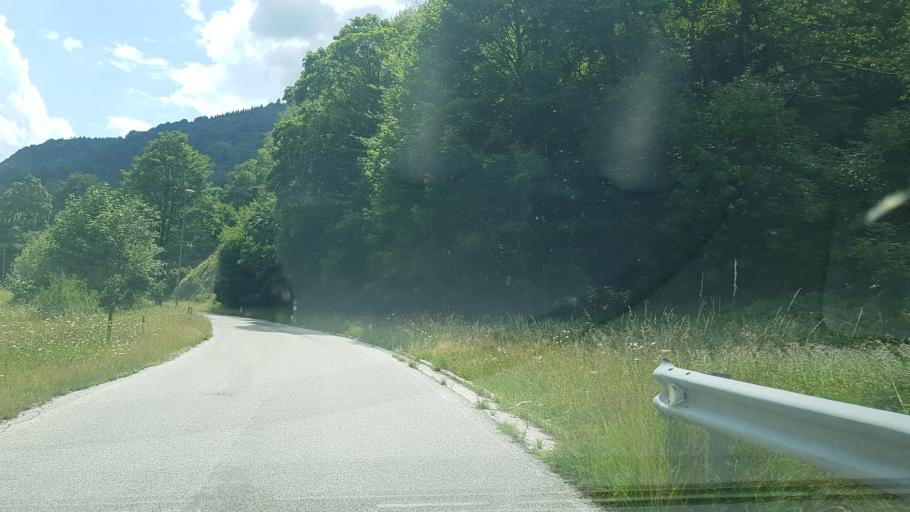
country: IT
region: Friuli Venezia Giulia
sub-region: Provincia di Udine
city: Moggio Udinese
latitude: 46.4819
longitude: 13.1893
